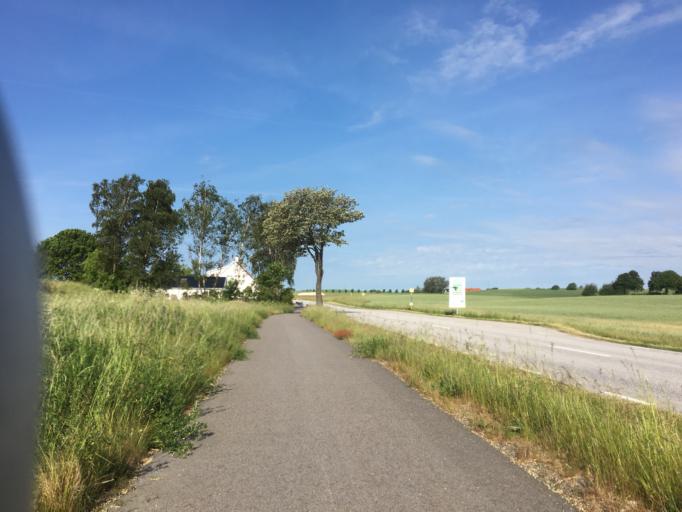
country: SE
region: Skane
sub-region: Skurups Kommun
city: Rydsgard
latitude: 55.4183
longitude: 13.6468
